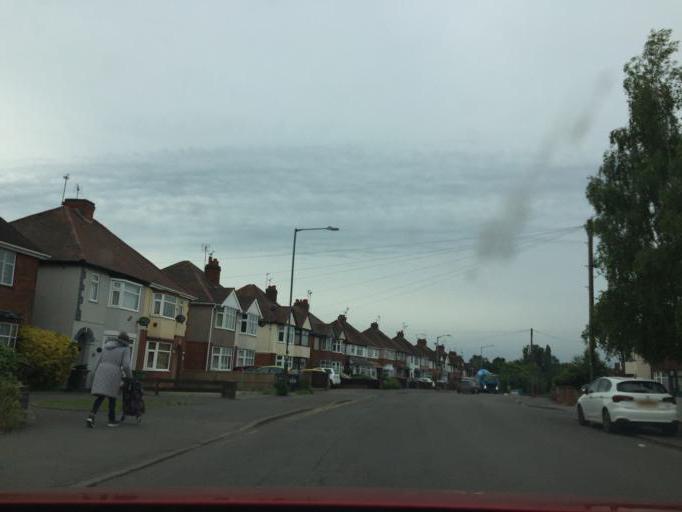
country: GB
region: England
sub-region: Warwickshire
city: Nuneaton
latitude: 52.5208
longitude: -1.4838
